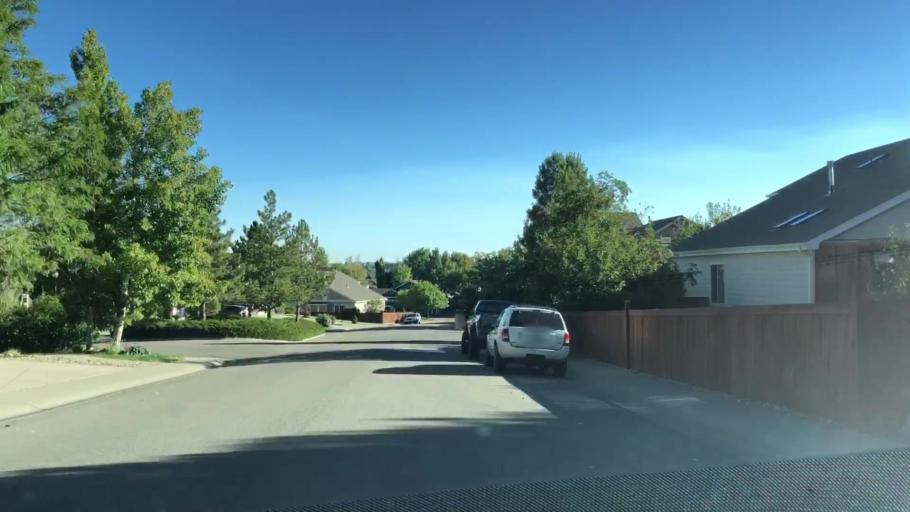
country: US
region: Colorado
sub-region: Larimer County
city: Loveland
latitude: 40.3973
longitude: -105.1375
